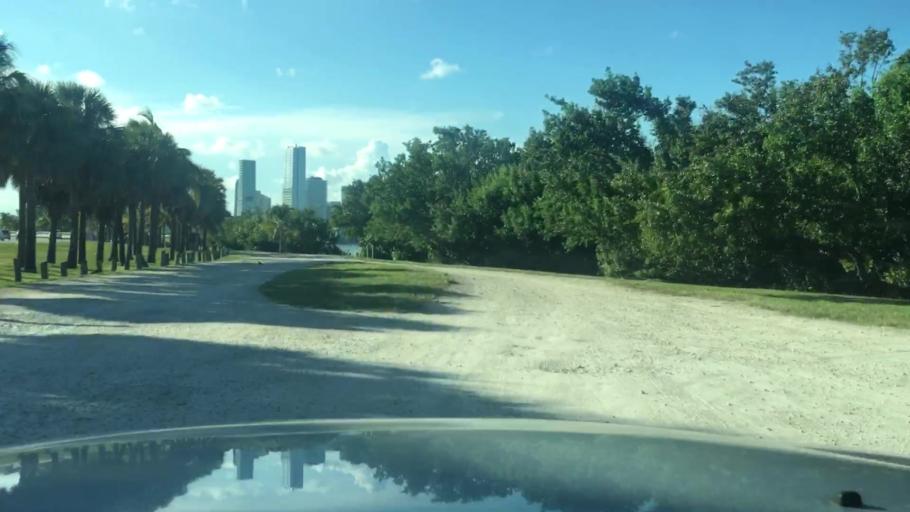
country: US
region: Florida
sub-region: Miami-Dade County
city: Miami
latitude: 25.7455
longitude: -80.1750
